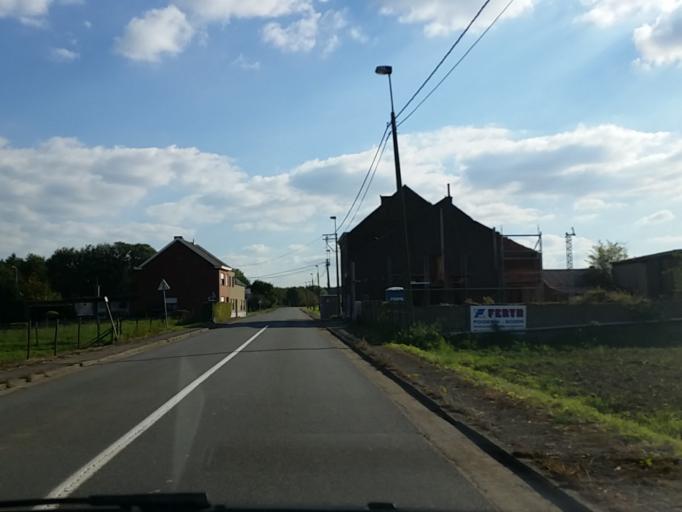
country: BE
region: Flanders
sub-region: Provincie Vlaams-Brabant
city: Bertem
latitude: 50.9176
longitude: 4.6142
